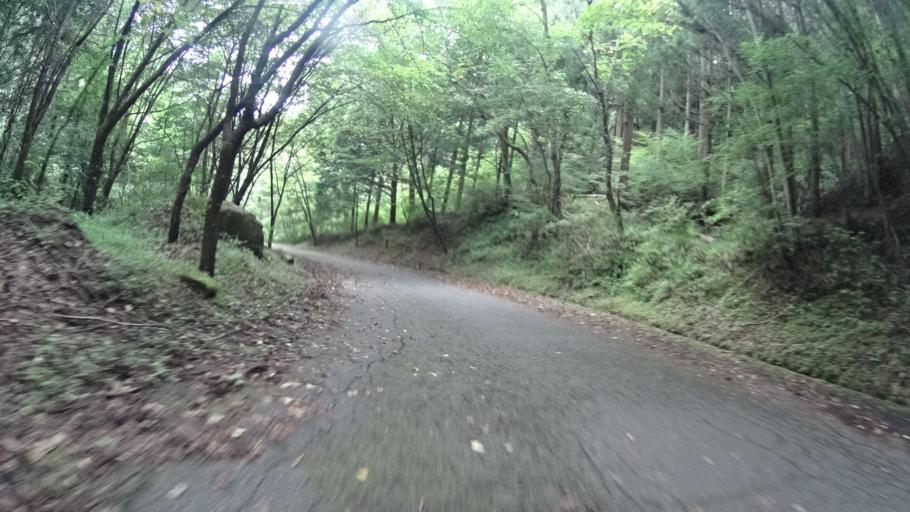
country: JP
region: Yamanashi
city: Kofu-shi
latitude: 35.8085
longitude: 138.5881
